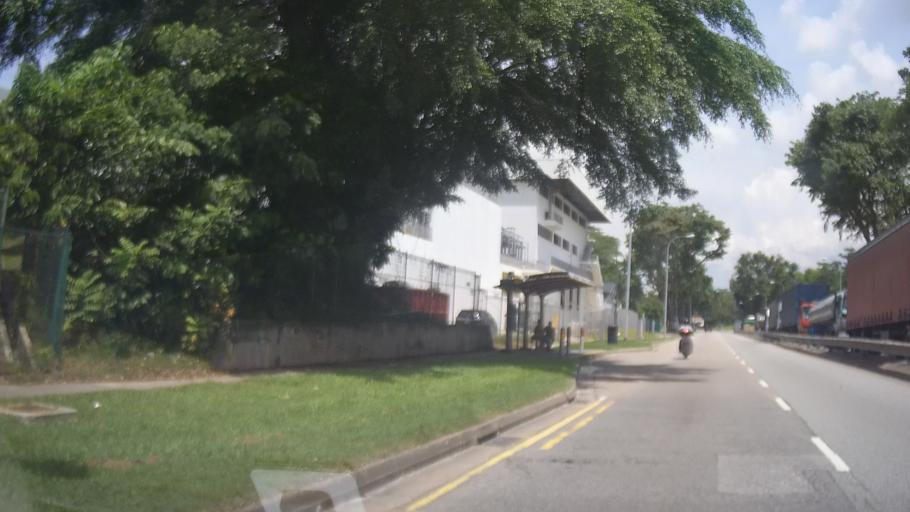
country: MY
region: Johor
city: Johor Bahru
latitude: 1.4371
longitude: 103.7648
